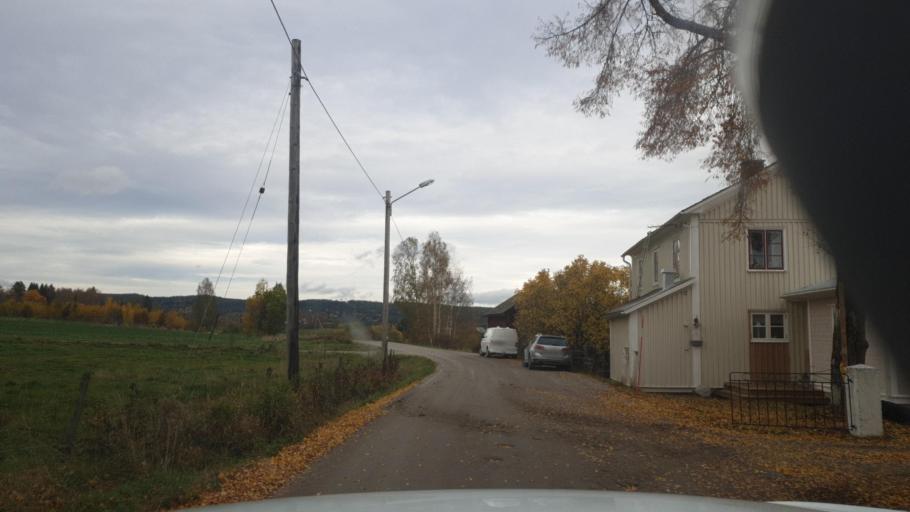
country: SE
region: Vaermland
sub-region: Arvika Kommun
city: Arvika
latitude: 59.6672
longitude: 12.7587
